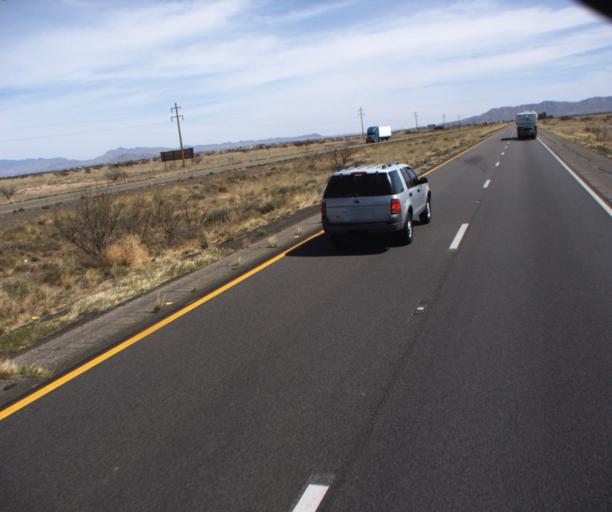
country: US
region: Arizona
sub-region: Cochise County
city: Willcox
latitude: 32.2082
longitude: -109.8957
